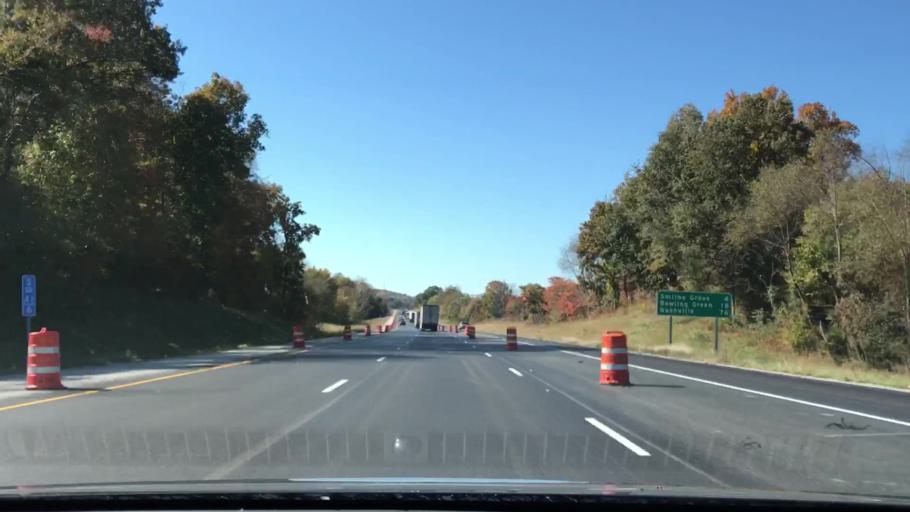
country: US
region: Kentucky
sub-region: Edmonson County
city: Brownsville
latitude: 37.0534
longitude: -86.1370
